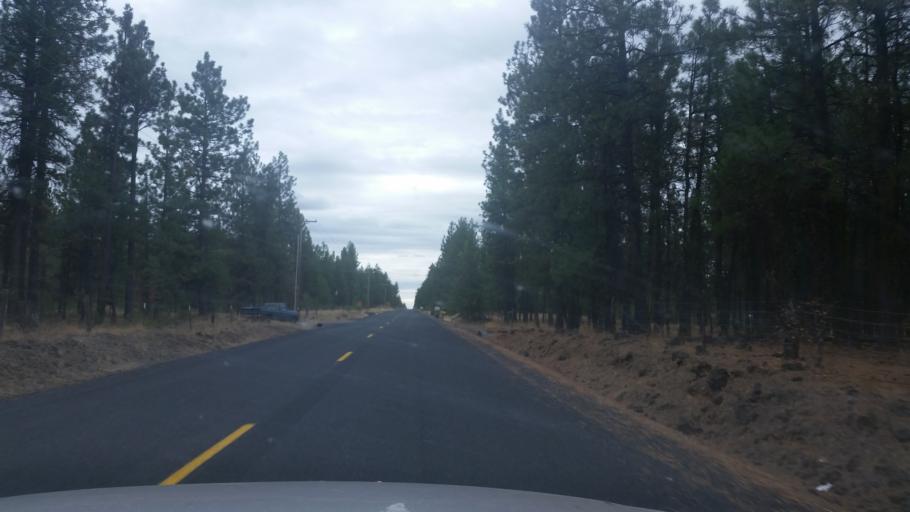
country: US
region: Washington
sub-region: Spokane County
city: Medical Lake
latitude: 47.4778
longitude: -117.7792
